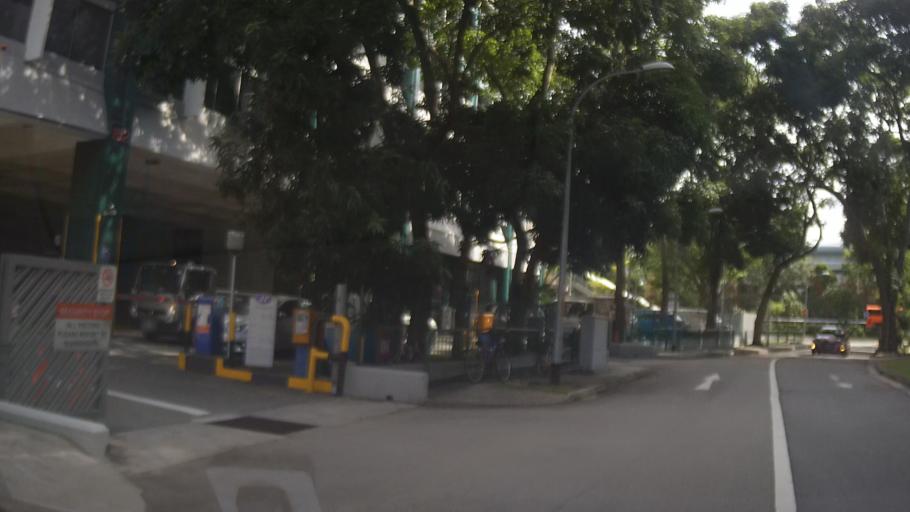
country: SG
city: Singapore
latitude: 1.3291
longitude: 103.8906
